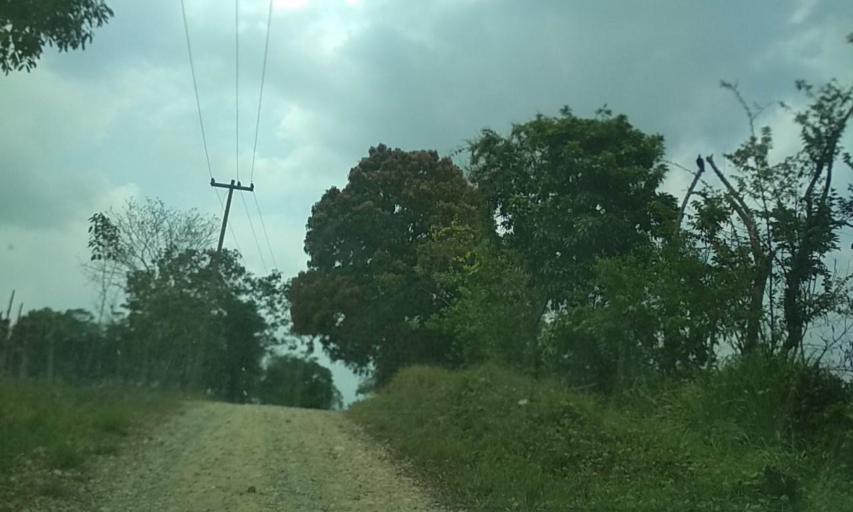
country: MX
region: Tabasco
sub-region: Huimanguillo
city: Francisco Rueda
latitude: 17.5898
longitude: -93.7936
